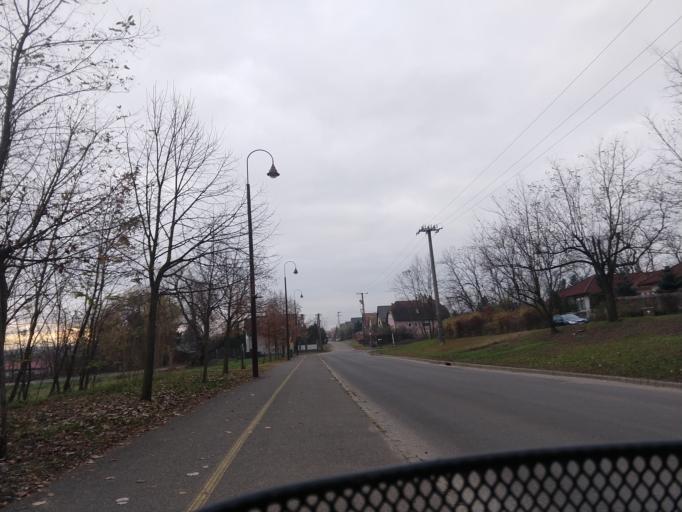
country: HU
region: Pest
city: Veresegyhaz
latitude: 47.6602
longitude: 19.2761
